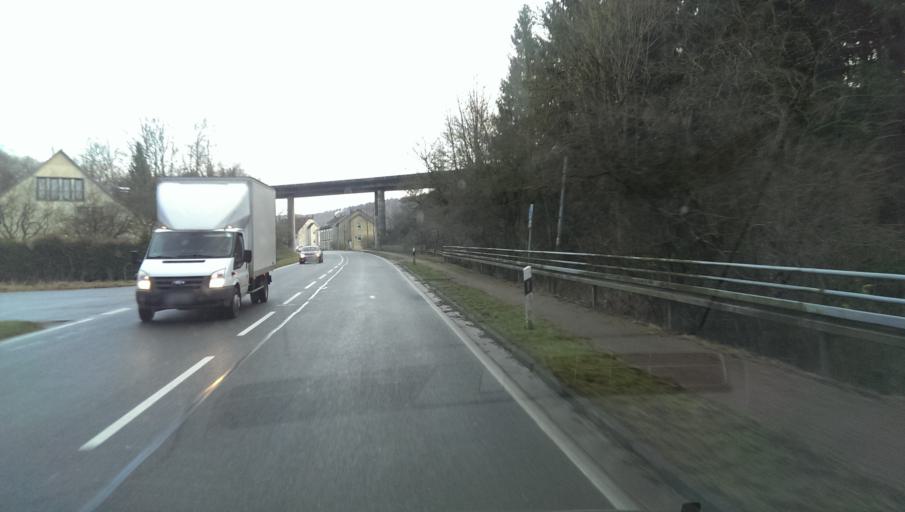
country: DE
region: Lower Saxony
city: Lenne
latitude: 51.8987
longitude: 9.6945
